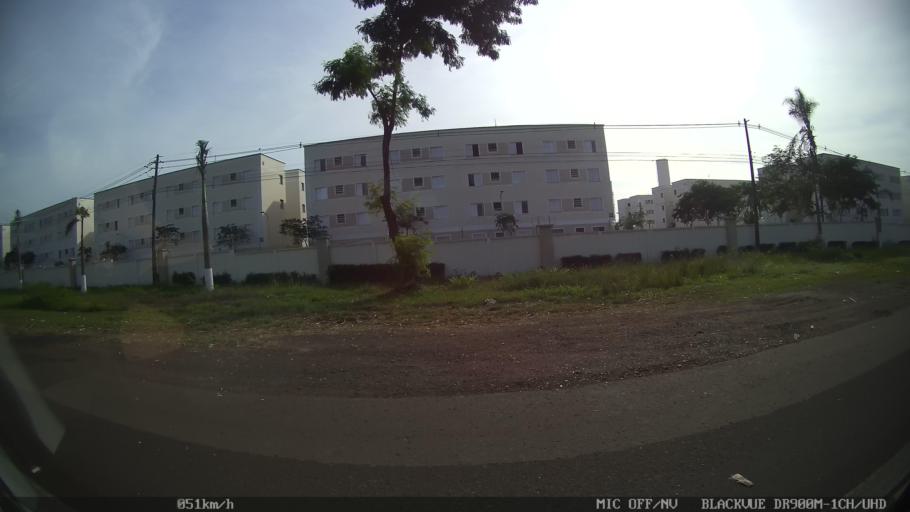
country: BR
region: Sao Paulo
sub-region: Piracicaba
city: Piracicaba
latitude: -22.6844
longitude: -47.6799
